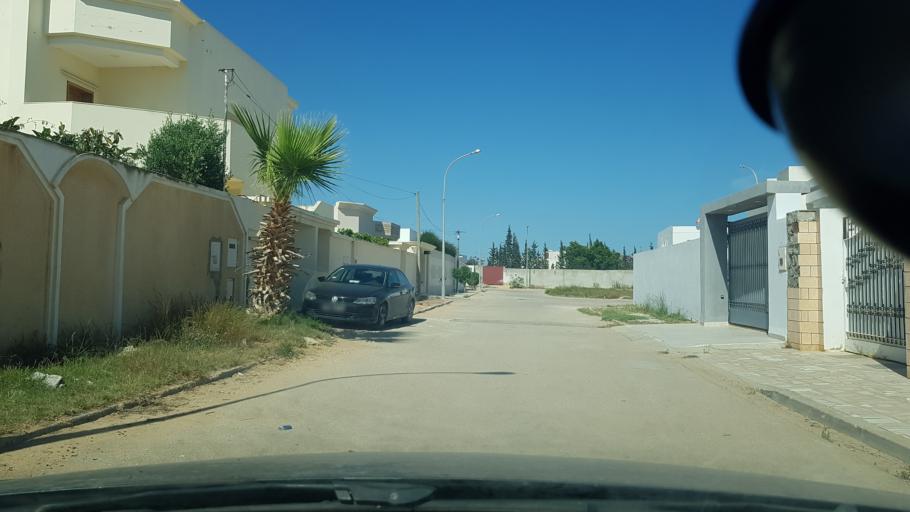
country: TN
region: Safaqis
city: Al Qarmadah
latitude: 34.8299
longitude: 10.7594
